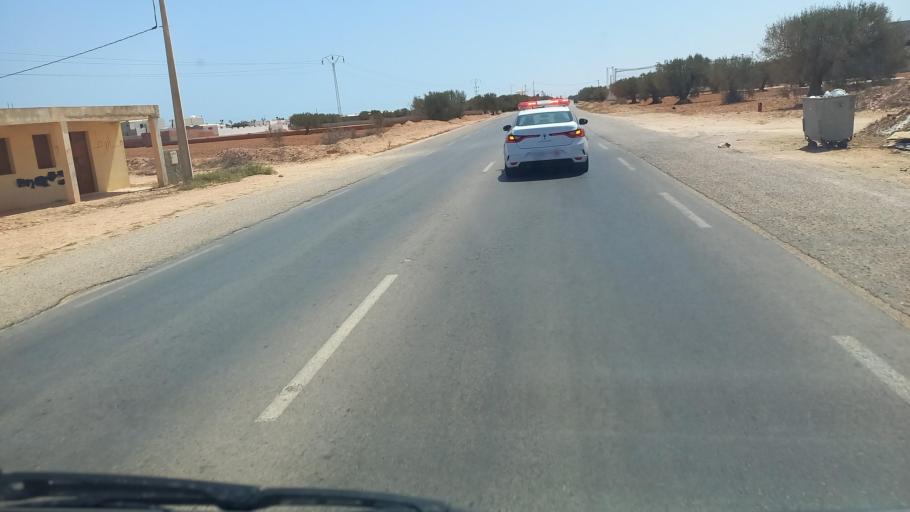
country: TN
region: Madanin
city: Zarzis
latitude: 33.5476
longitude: 11.0701
